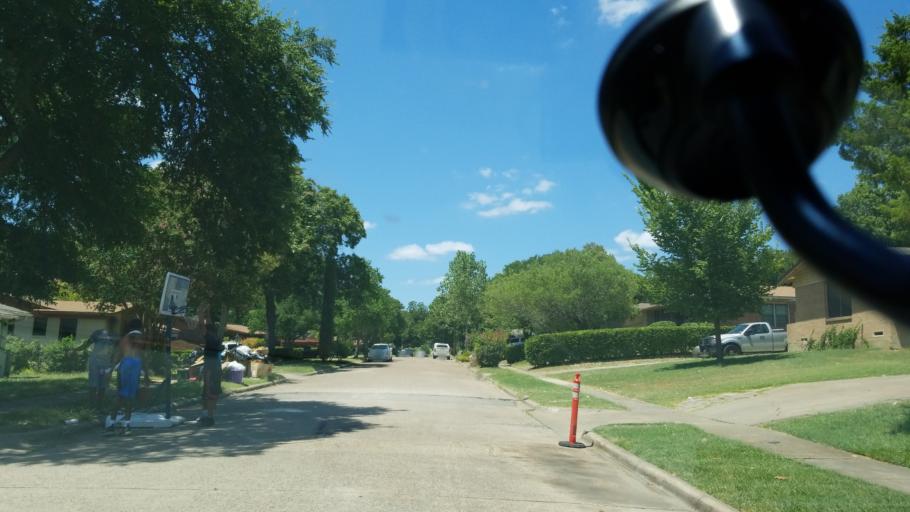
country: US
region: Texas
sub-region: Dallas County
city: Cockrell Hill
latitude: 32.6937
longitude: -96.8176
